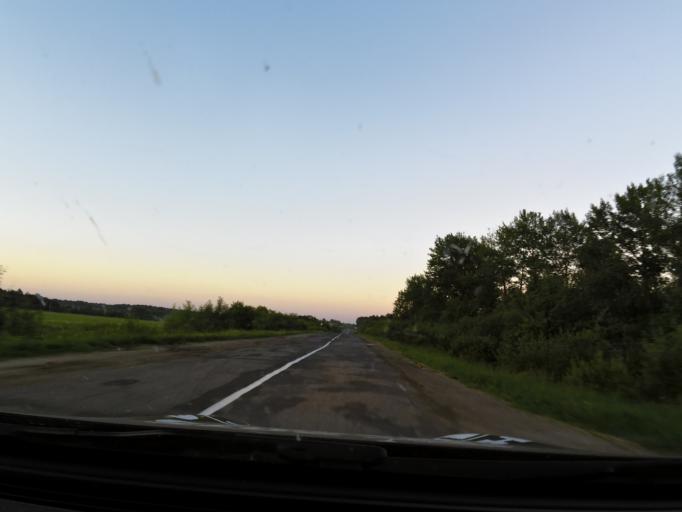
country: RU
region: Jaroslavl
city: Lyubim
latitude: 58.3236
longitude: 41.0274
